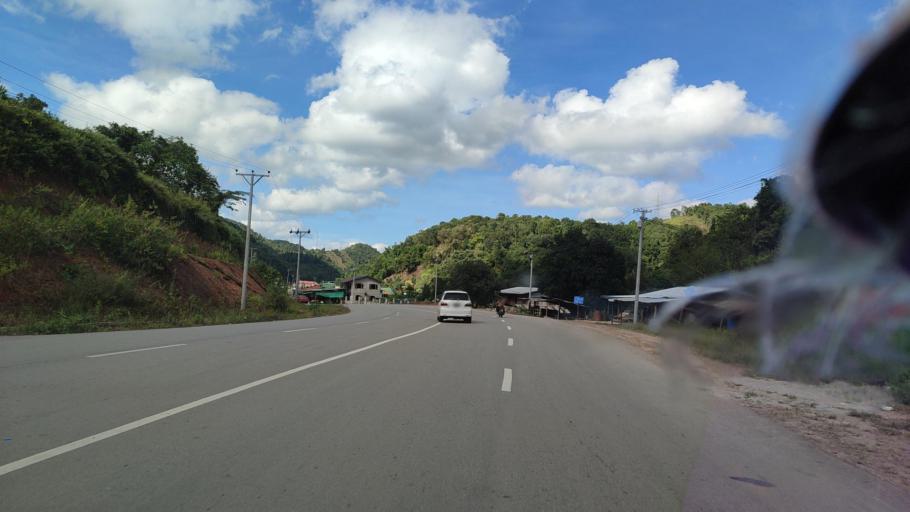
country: MM
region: Mandalay
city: Yamethin
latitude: 20.6626
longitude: 96.5366
